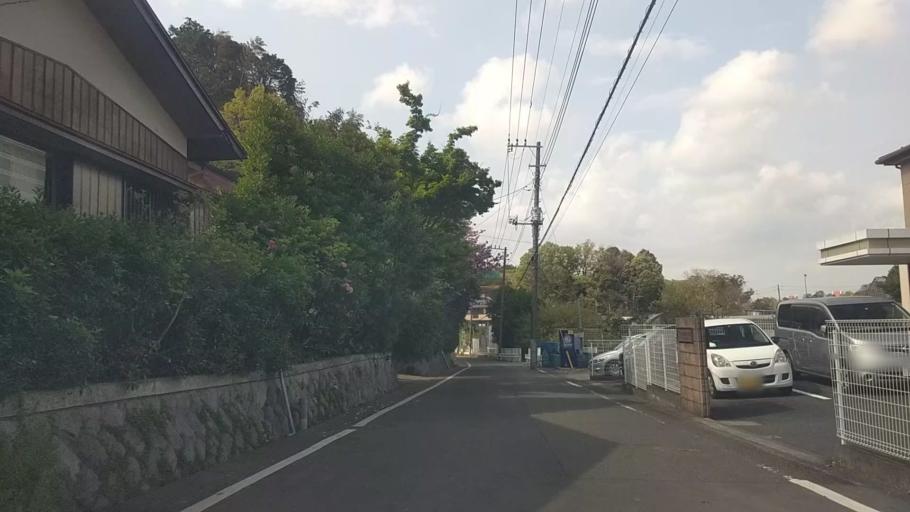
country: JP
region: Kanagawa
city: Kamakura
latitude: 35.3797
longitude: 139.5634
